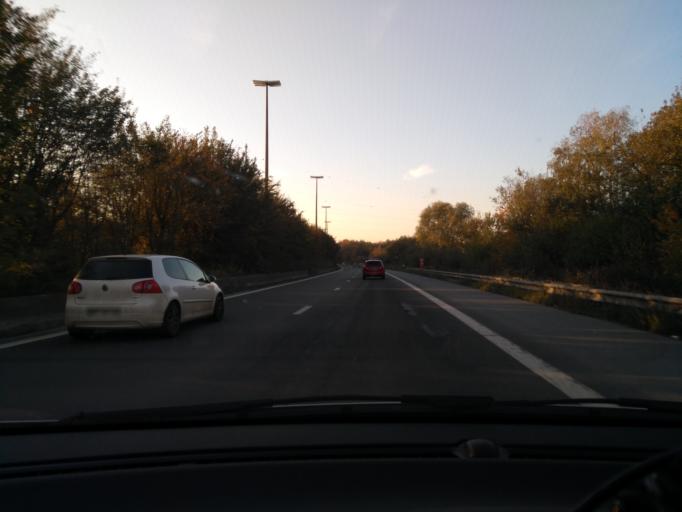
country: BE
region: Wallonia
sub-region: Province du Hainaut
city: Antoing
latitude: 50.5907
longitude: 3.4710
